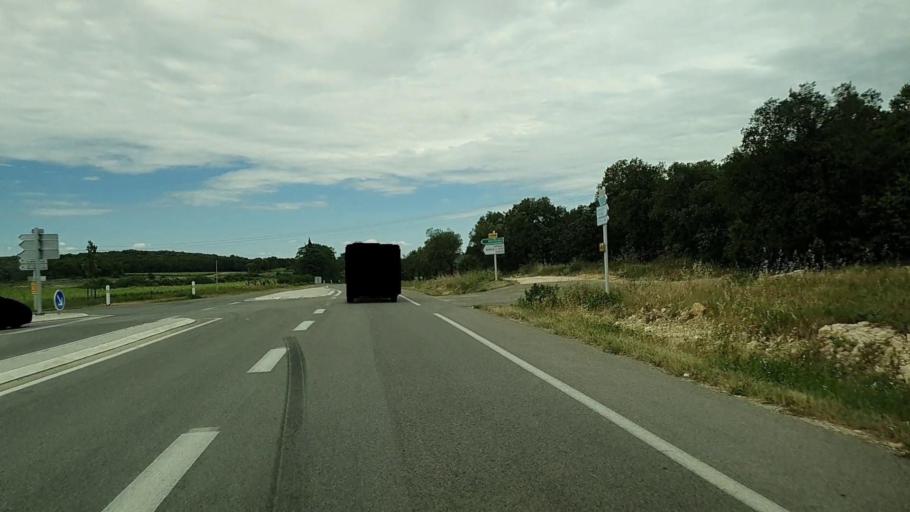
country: FR
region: Languedoc-Roussillon
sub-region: Departement du Gard
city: Connaux
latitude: 44.0560
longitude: 4.5710
